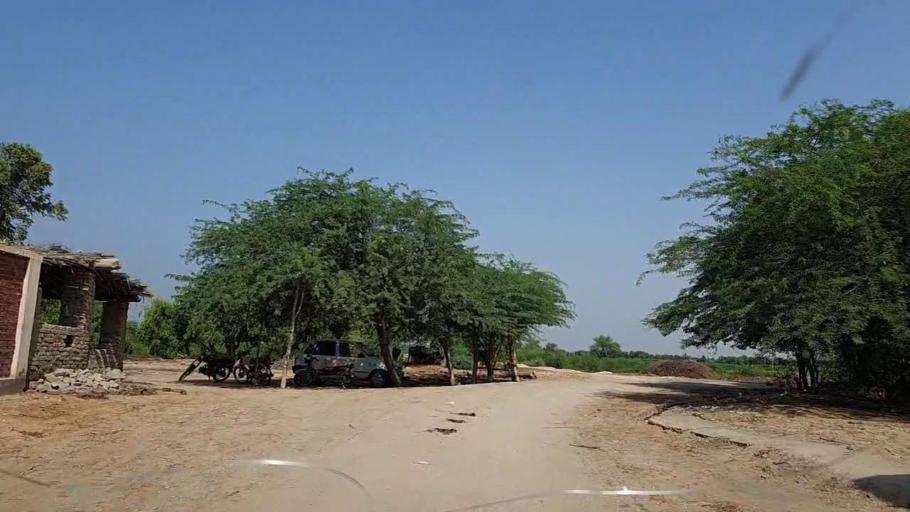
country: PK
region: Sindh
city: Khanpur
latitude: 27.7499
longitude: 69.3395
